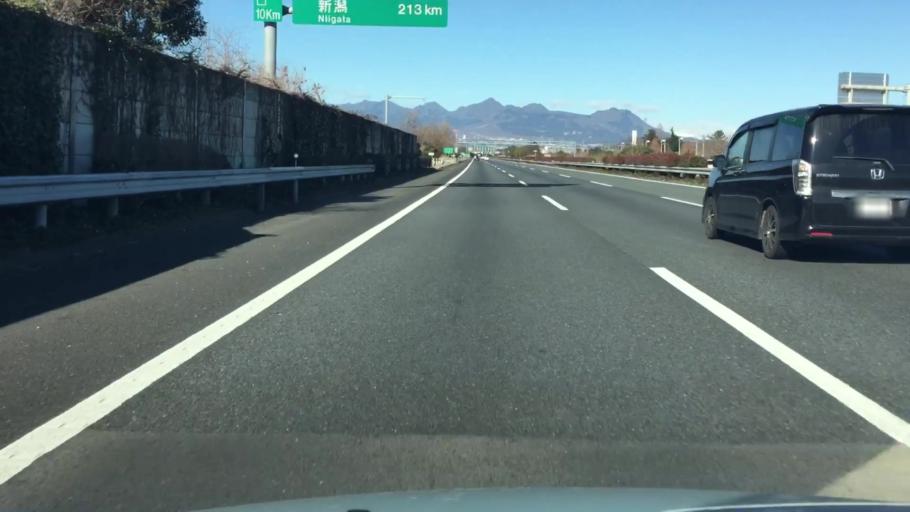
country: JP
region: Gunma
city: Takasaki
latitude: 36.3466
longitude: 139.0515
